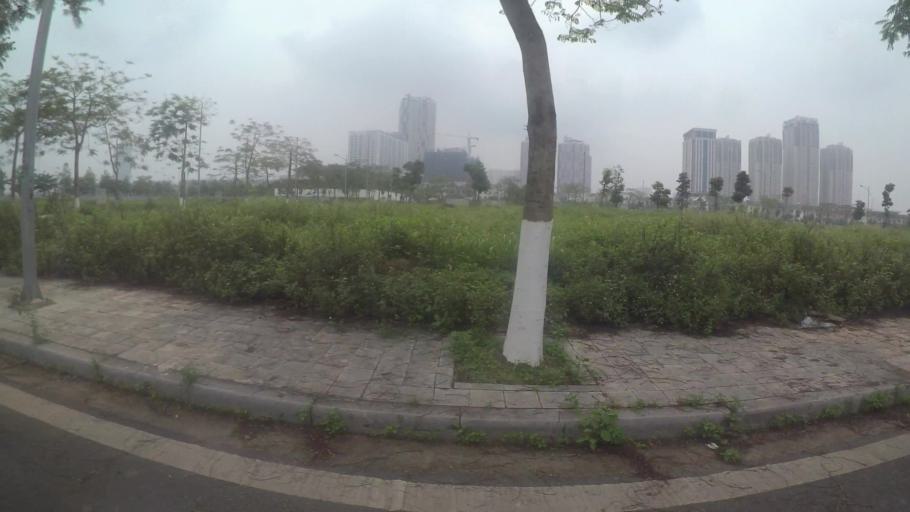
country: VN
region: Ha Noi
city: Ha Dong
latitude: 20.9791
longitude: 105.7563
